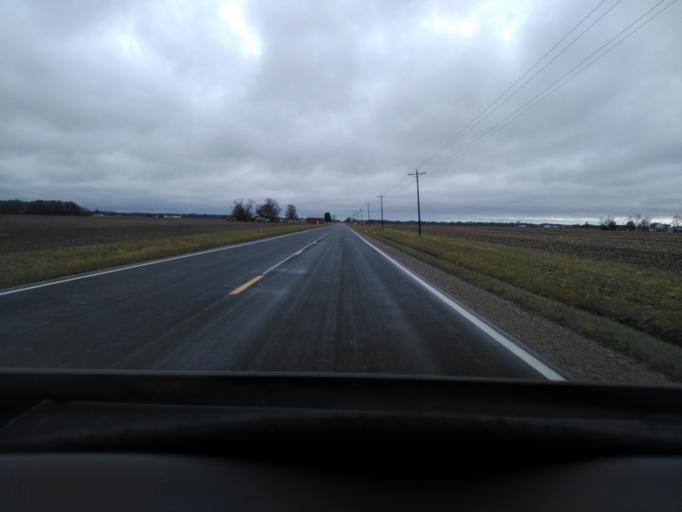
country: US
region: Illinois
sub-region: Effingham County
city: Altamont
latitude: 39.0206
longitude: -88.7484
